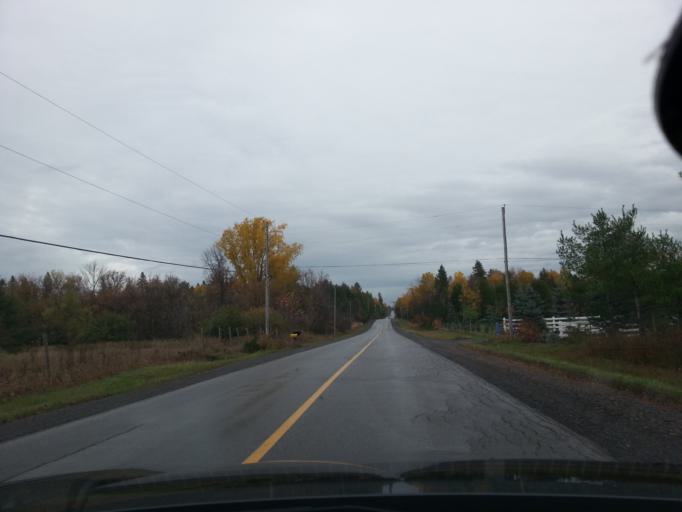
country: CA
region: Ontario
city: Bells Corners
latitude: 45.2283
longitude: -75.9435
